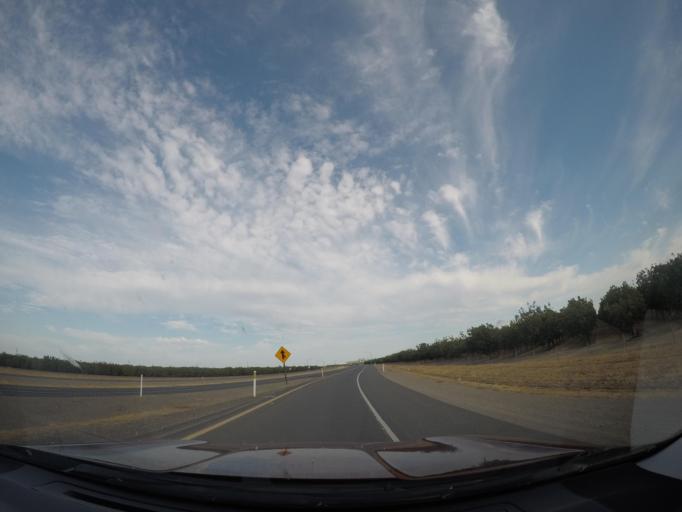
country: US
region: California
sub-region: Colusa County
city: Arbuckle
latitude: 39.0554
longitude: -122.0855
